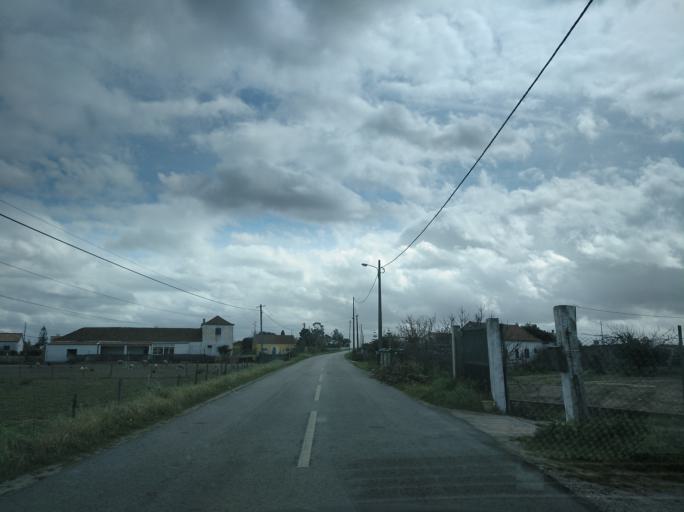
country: PT
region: Setubal
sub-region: Palmela
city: Pinhal Novo
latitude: 38.6736
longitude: -8.9163
